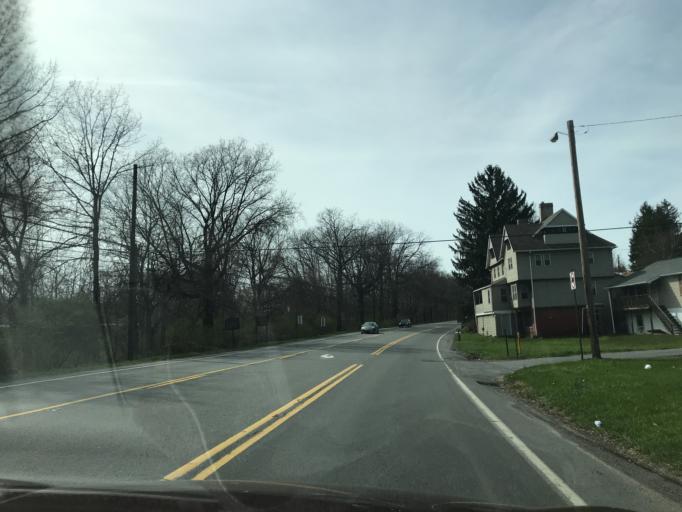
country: US
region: Pennsylvania
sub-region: Northumberland County
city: Northumberland
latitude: 40.8945
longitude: -76.8092
